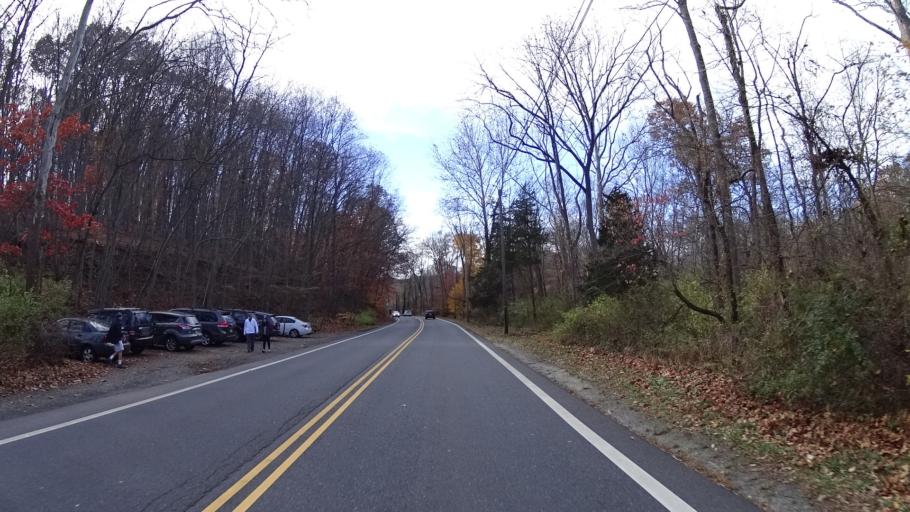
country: US
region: New Jersey
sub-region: Morris County
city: Mendham
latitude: 40.7888
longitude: -74.5461
